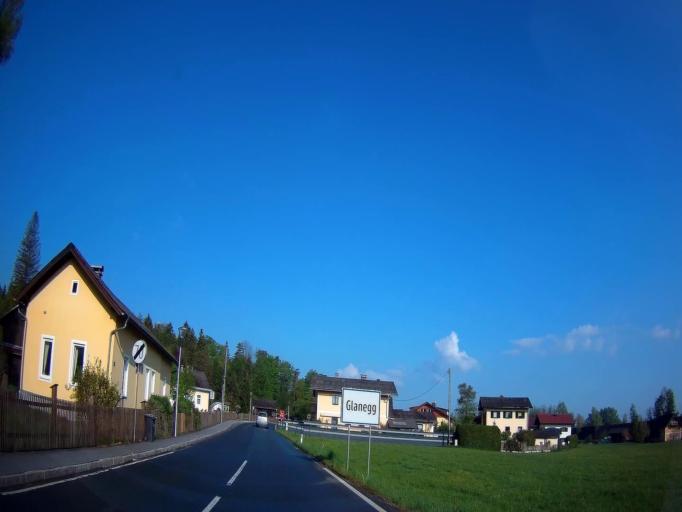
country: AT
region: Salzburg
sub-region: Politischer Bezirk Salzburg-Umgebung
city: Grodig
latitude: 47.7477
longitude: 13.0188
